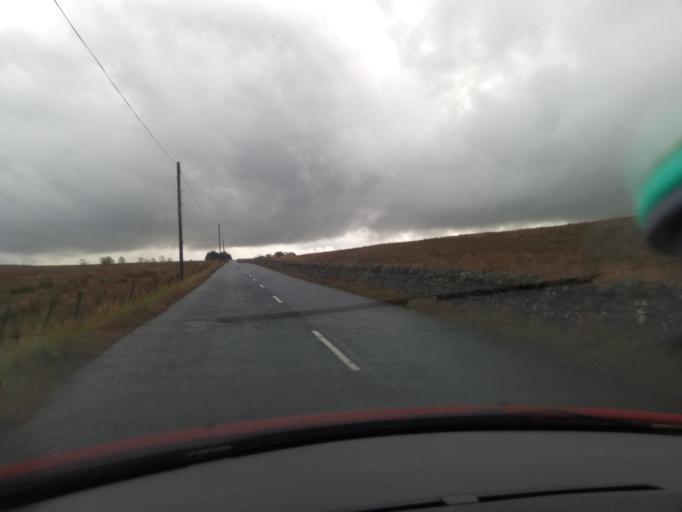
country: GB
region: England
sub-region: Northumberland
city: Birtley
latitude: 55.1310
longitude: -2.2447
